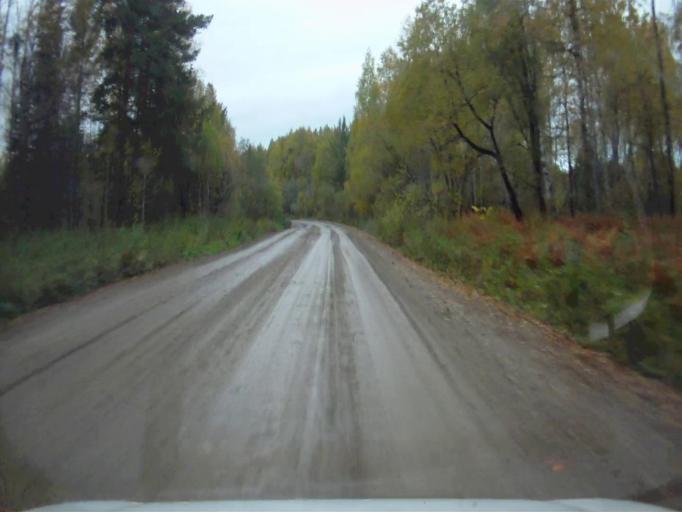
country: RU
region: Chelyabinsk
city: Nyazepetrovsk
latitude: 56.1041
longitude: 59.3856
